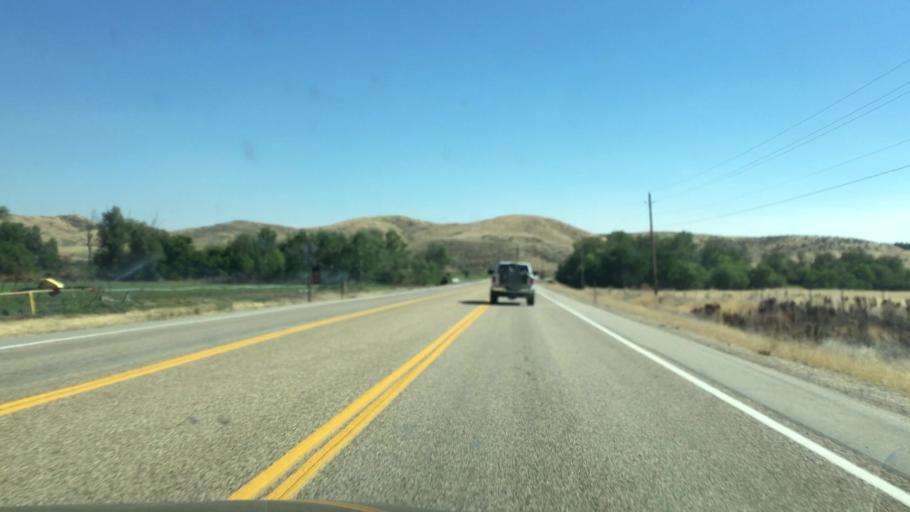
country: US
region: Idaho
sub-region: Ada County
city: Eagle
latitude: 43.7346
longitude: -116.3042
